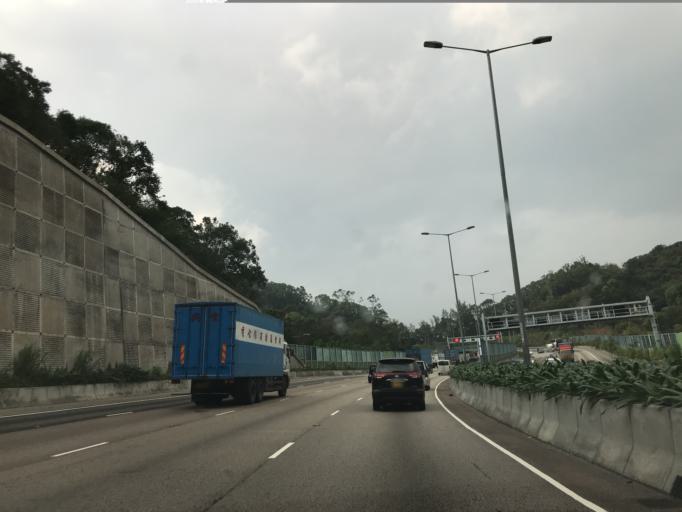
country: HK
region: Tai Po
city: Tai Po
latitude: 22.4415
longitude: 114.1590
